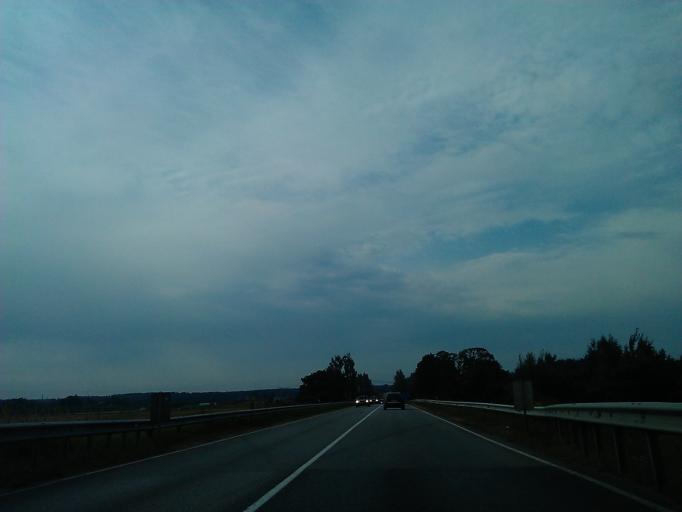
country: LV
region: Salaspils
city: Salaspils
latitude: 56.8526
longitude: 24.4000
